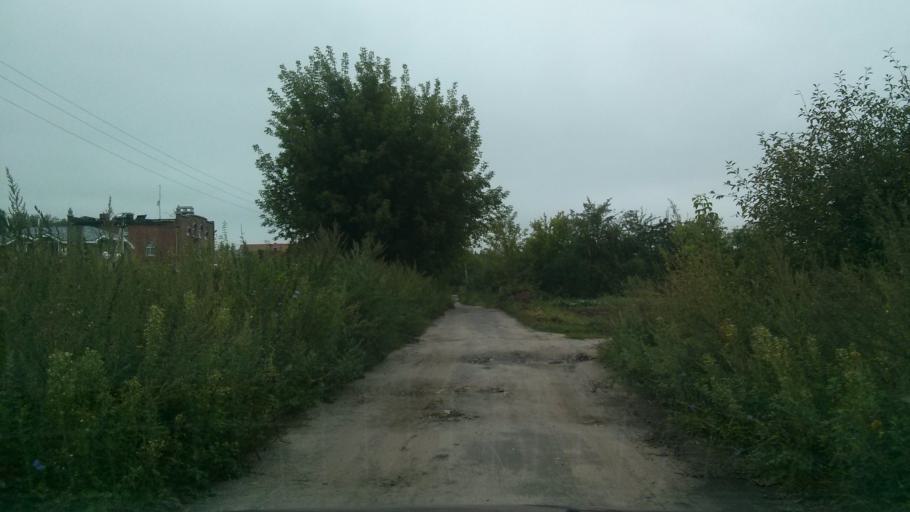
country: RU
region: Vladimir
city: Murom
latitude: 55.6041
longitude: 42.0309
